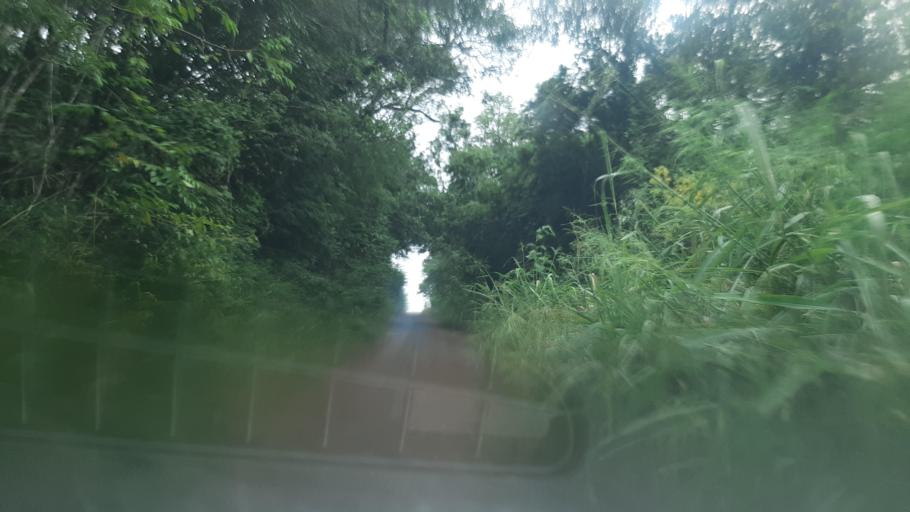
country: BR
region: Parana
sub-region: Ampere
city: Ampere
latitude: -26.0499
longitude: -53.5282
